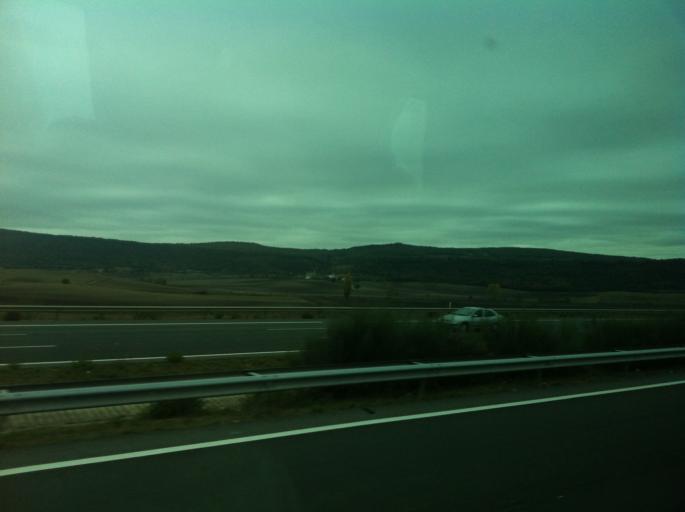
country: ES
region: Basque Country
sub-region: Provincia de Alava
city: Arminon
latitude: 42.7552
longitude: -2.8285
